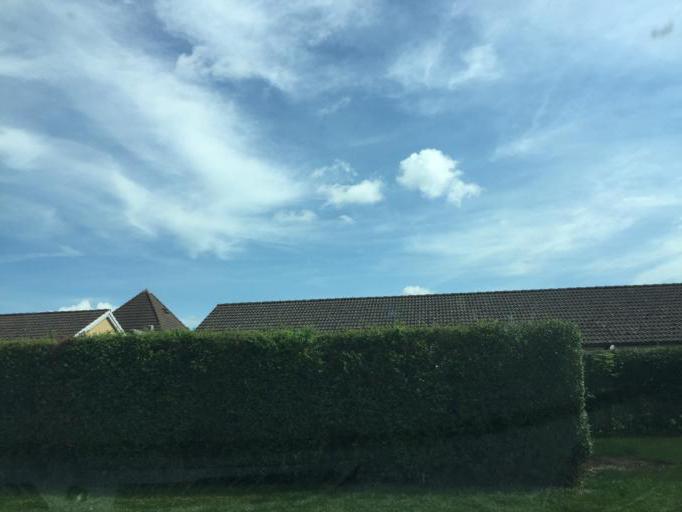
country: DK
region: South Denmark
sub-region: Odense Kommune
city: Hojby
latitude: 55.3332
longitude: 10.4430
